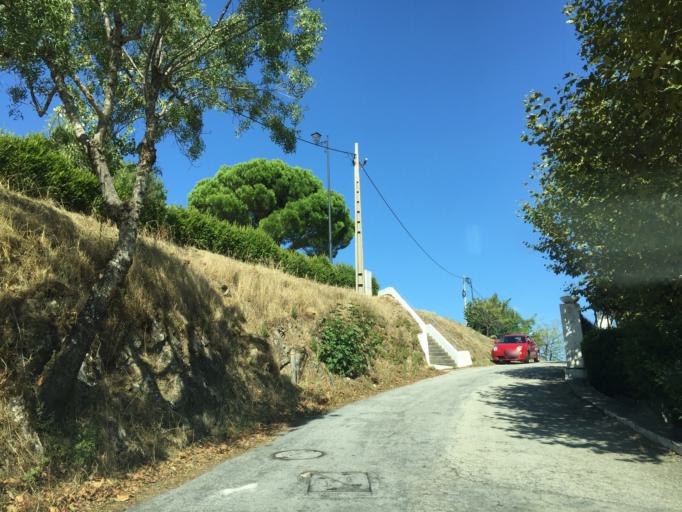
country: PT
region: Portalegre
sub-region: Marvao
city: Marvao
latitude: 39.3933
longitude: -7.3732
